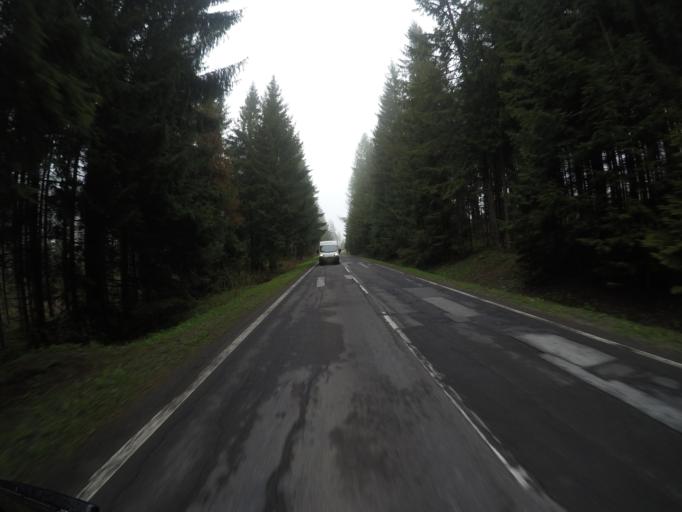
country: SK
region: Presovsky
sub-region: Okres Poprad
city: Strba
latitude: 49.1042
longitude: 20.0586
